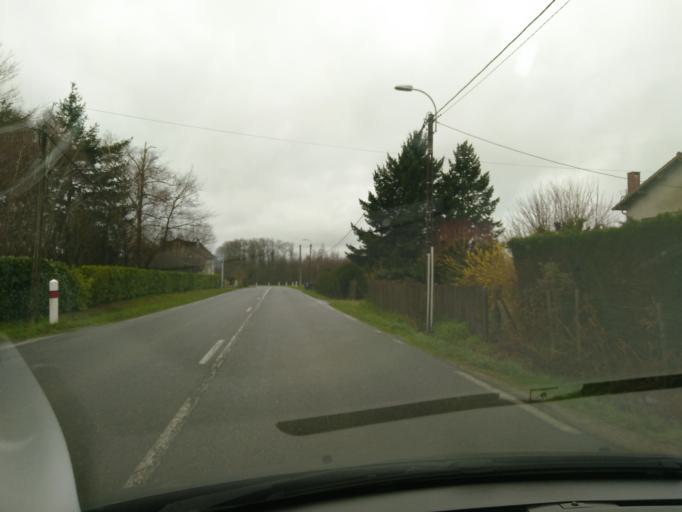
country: FR
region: Limousin
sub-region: Departement de la Haute-Vienne
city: Solignac
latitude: 45.7192
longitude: 1.2505
